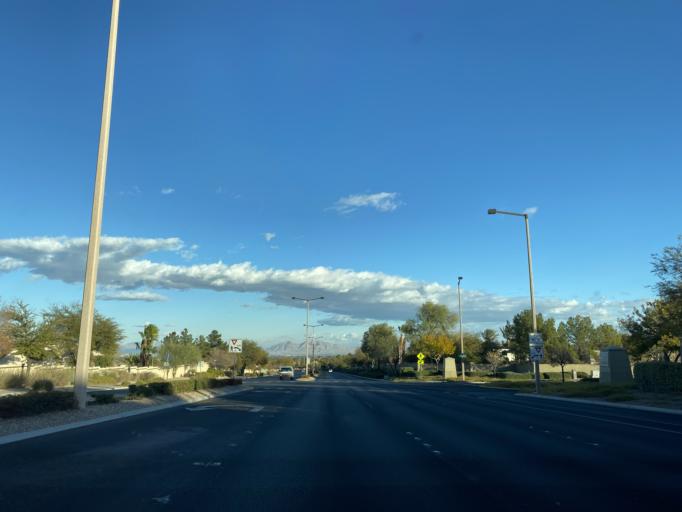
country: US
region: Nevada
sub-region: Clark County
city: Summerlin South
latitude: 36.2046
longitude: -115.3149
